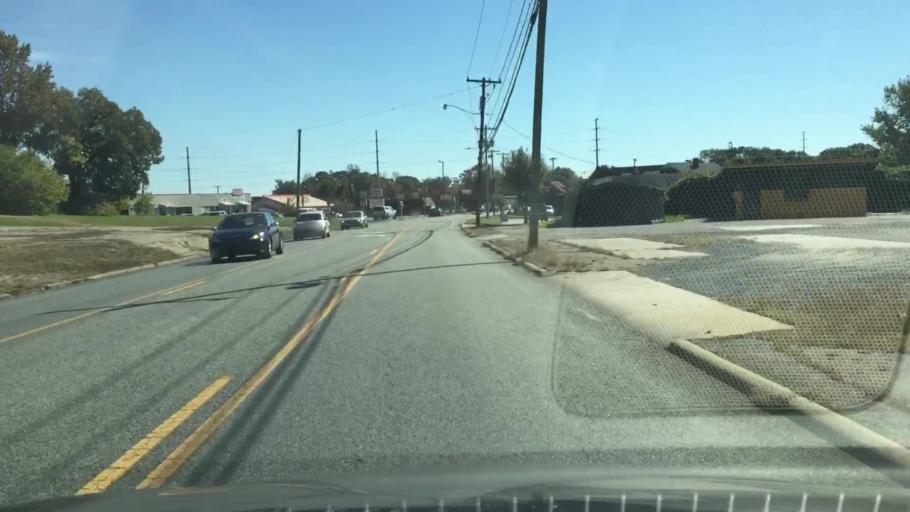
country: US
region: North Carolina
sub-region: Rockingham County
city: Reidsville
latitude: 36.3438
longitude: -79.6641
